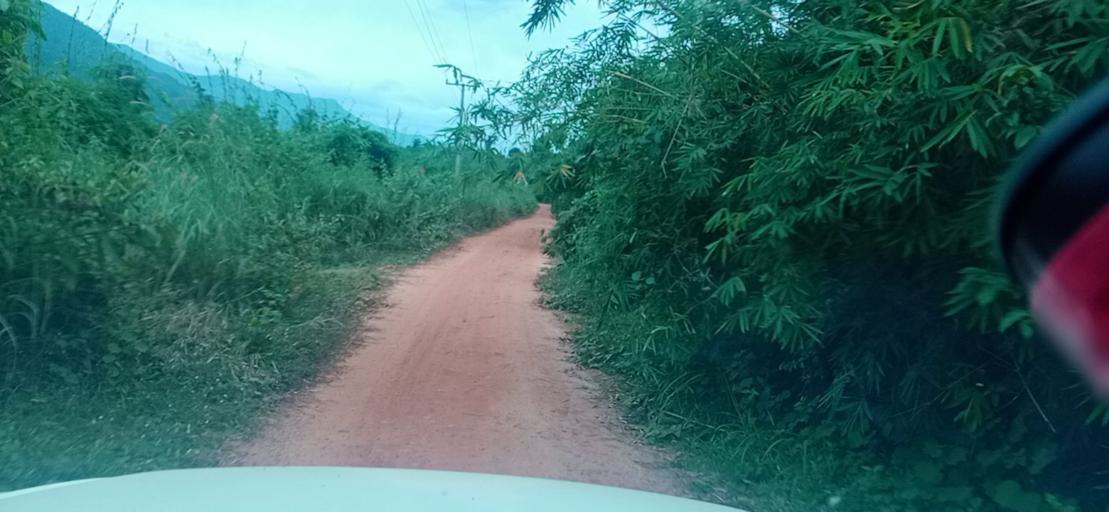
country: TH
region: Changwat Bueng Kan
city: Pak Khat
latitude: 18.5628
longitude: 103.2999
